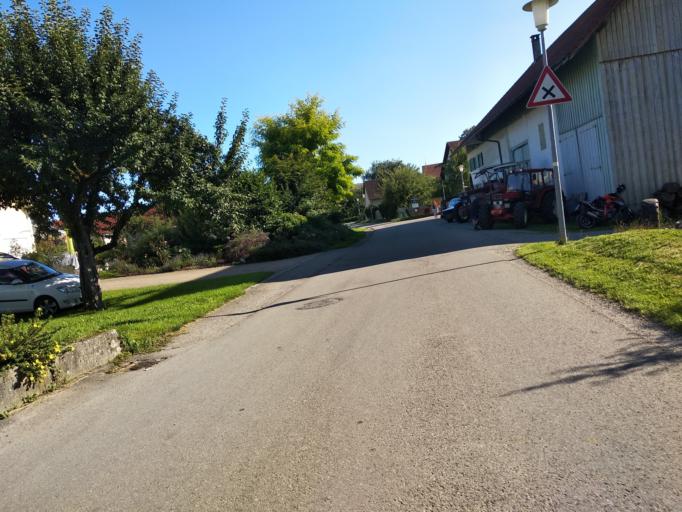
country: DE
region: Baden-Wuerttemberg
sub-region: Tuebingen Region
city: Leutkirch im Allgau
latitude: 47.7765
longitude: 10.0412
